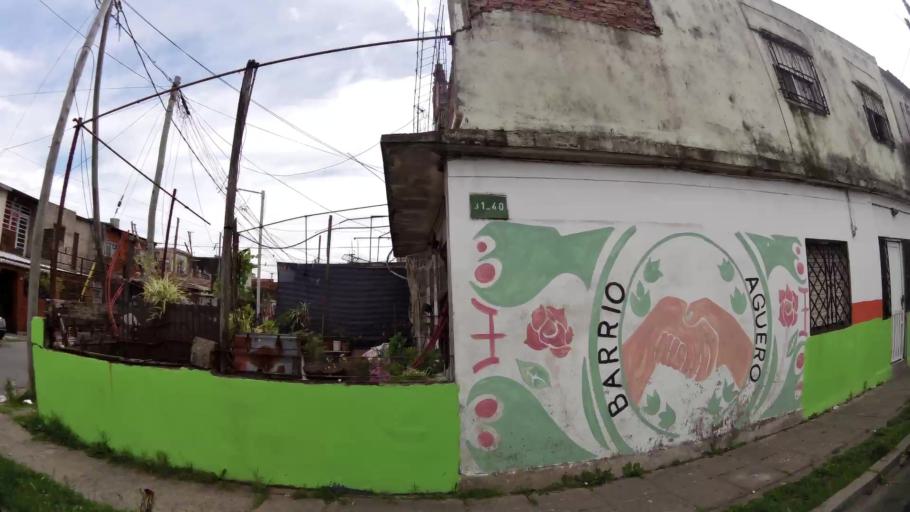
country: AR
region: Buenos Aires
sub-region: Partido de Avellaneda
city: Avellaneda
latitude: -34.6755
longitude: -58.3727
